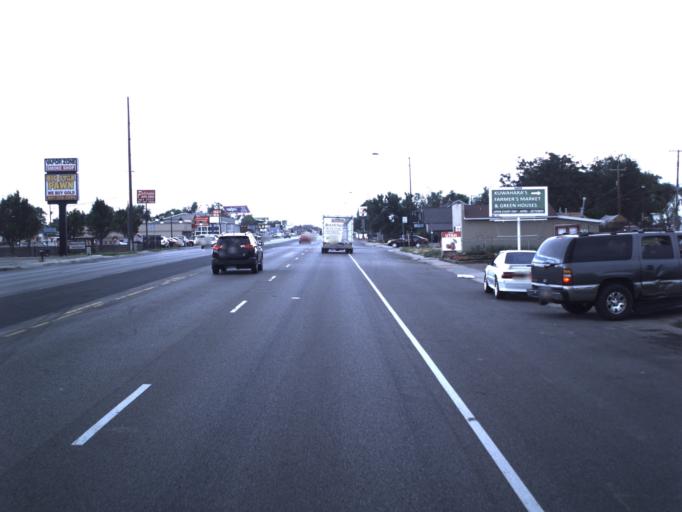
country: US
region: Utah
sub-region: Salt Lake County
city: Sandy City
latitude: 40.5954
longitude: -111.8908
